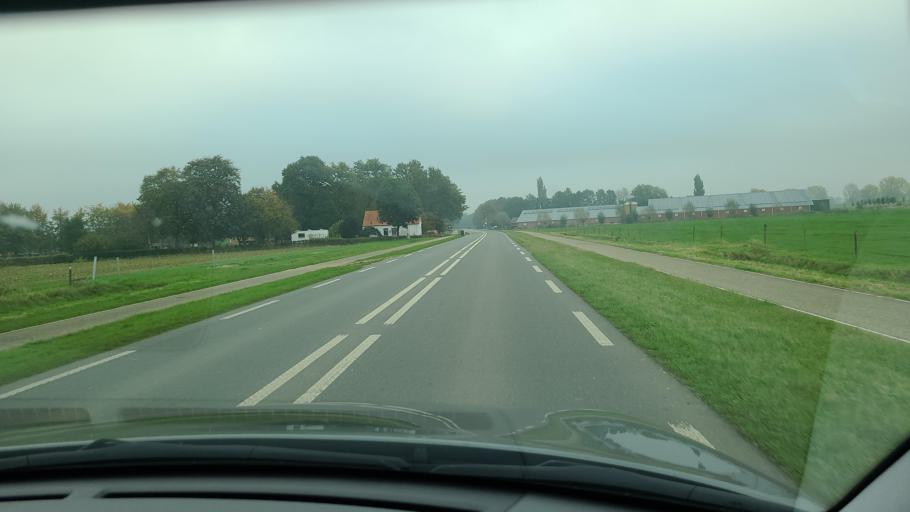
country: NL
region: North Brabant
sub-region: Gemeente Grave
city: Grave
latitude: 51.7600
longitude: 5.8039
